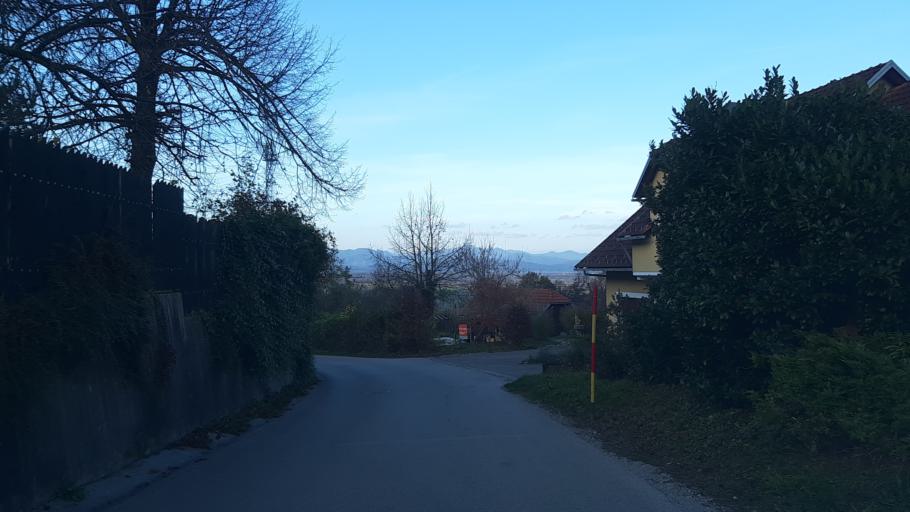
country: SI
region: Borovnica
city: Borovnica
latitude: 45.9248
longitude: 14.3530
